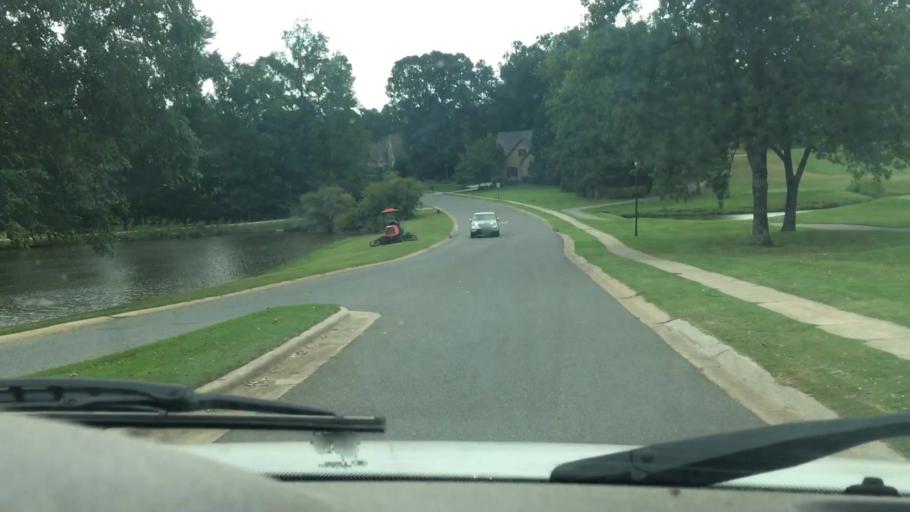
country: US
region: North Carolina
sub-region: Gaston County
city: Davidson
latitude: 35.4654
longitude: -80.8033
